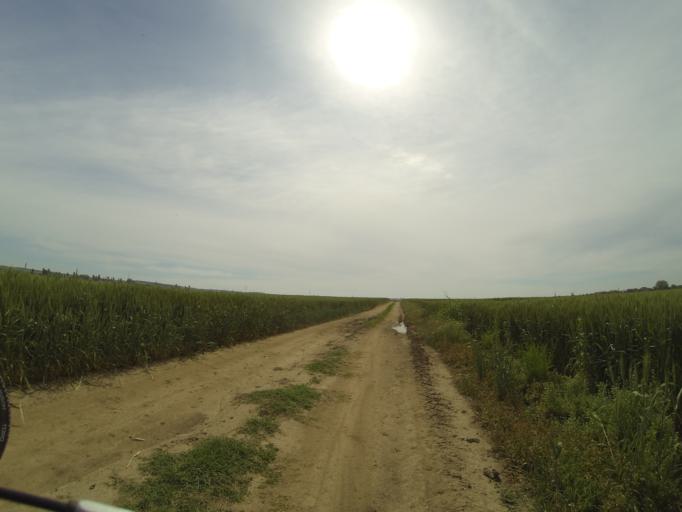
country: RO
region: Dolj
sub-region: Comuna Malu Mare
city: Preajba
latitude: 44.2694
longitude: 23.8574
